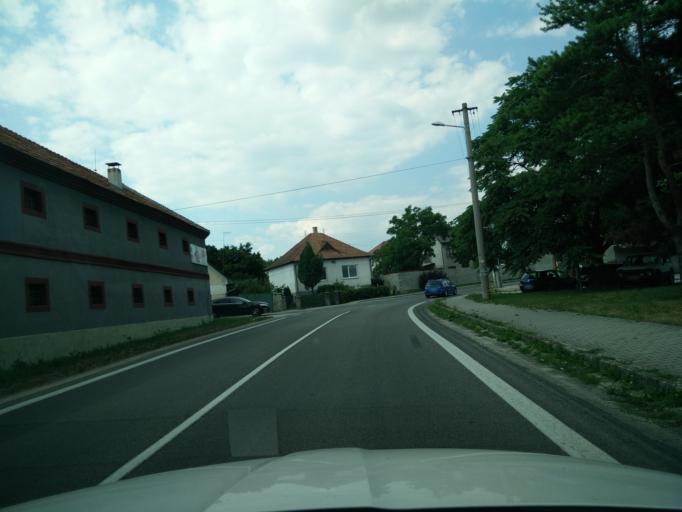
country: SK
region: Nitriansky
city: Partizanske
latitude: 48.6262
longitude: 18.3026
